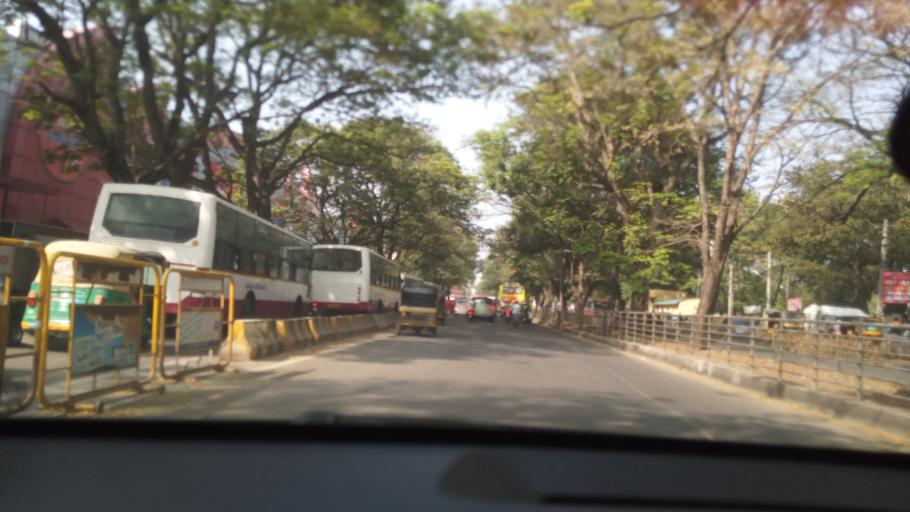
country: IN
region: Karnataka
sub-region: Mysore
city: Mysore
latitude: 12.3119
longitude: 76.6589
